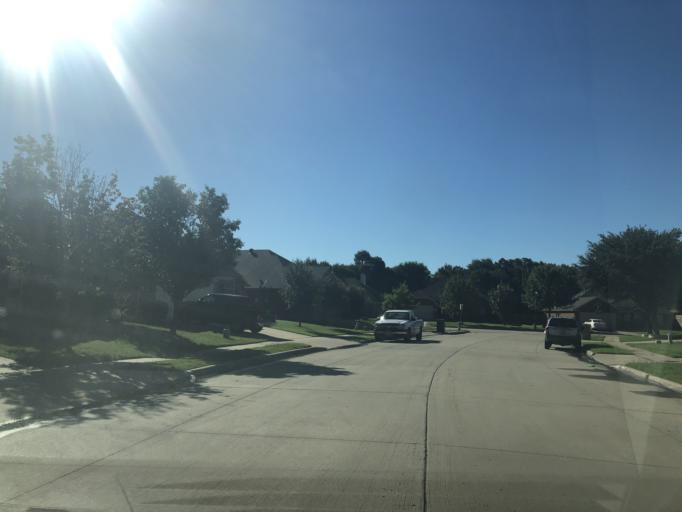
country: US
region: Texas
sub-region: Dallas County
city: Duncanville
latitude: 32.6588
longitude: -96.9690
